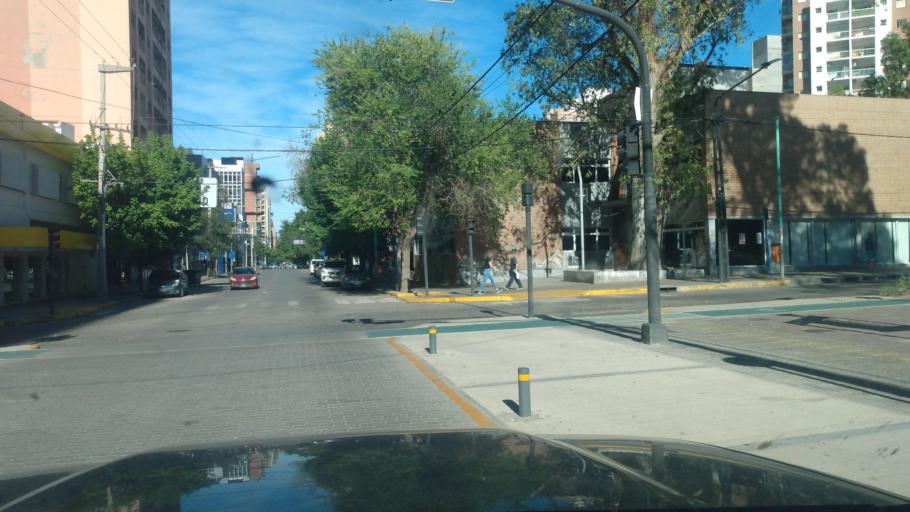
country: AR
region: Neuquen
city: Neuquen
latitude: -38.9528
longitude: -68.0591
